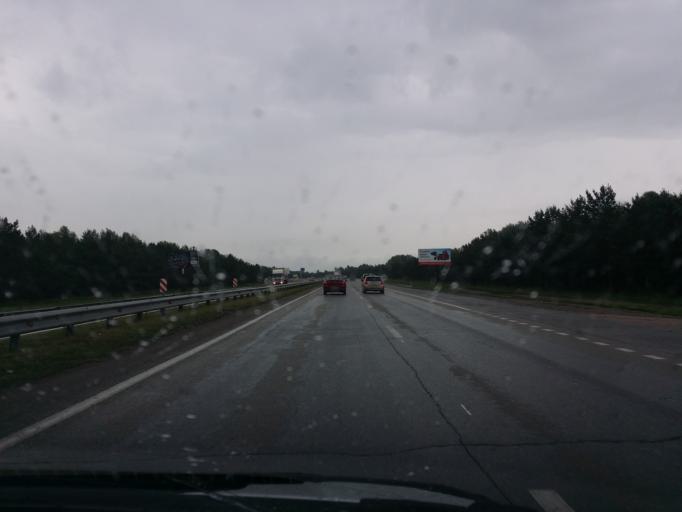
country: RU
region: Altai Krai
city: Zaton
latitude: 53.3150
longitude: 83.8508
